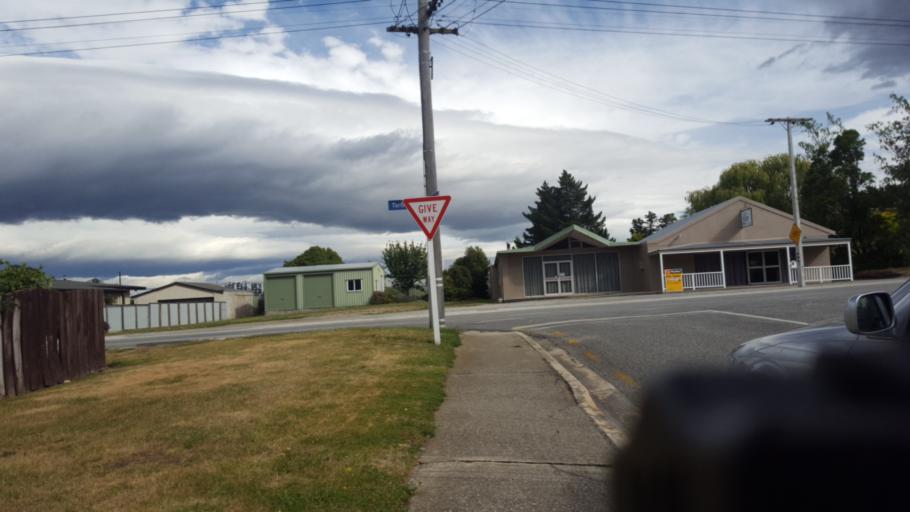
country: NZ
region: Otago
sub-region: Queenstown-Lakes District
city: Wanaka
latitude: -45.2483
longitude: 169.4003
